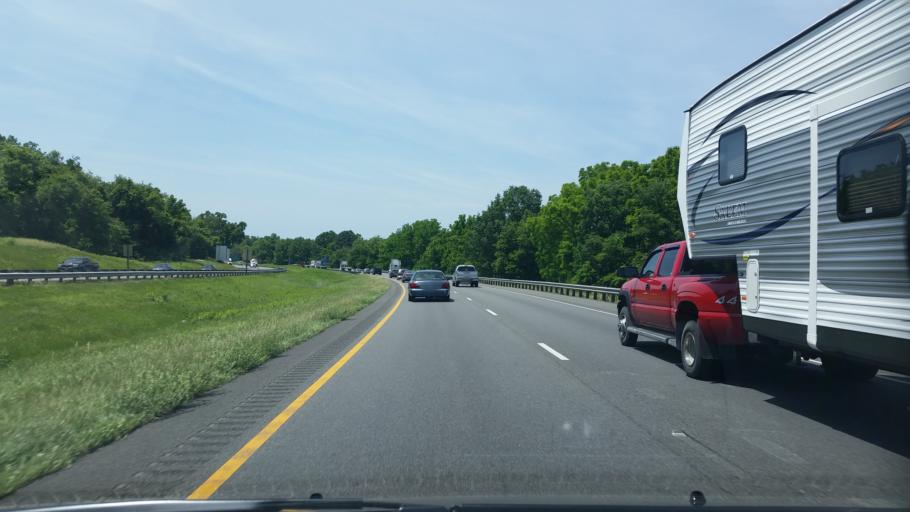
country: US
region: Maryland
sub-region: Washington County
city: Williamsport
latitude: 39.6144
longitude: -77.7952
